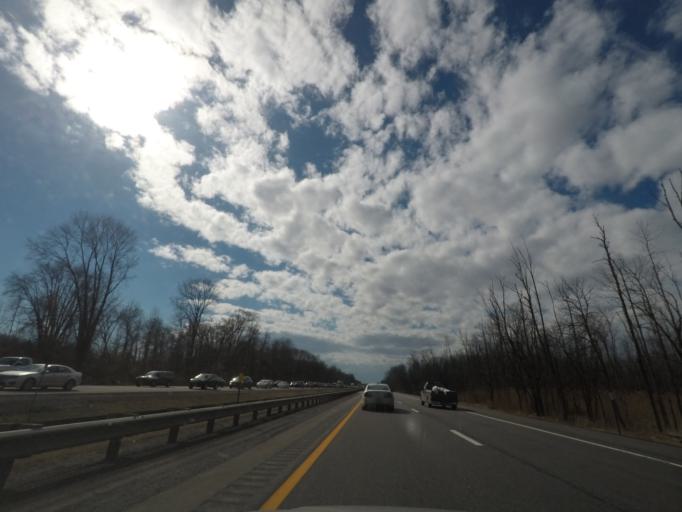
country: US
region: New York
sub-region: Madison County
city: Wampsville
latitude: 43.1046
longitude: -75.7001
